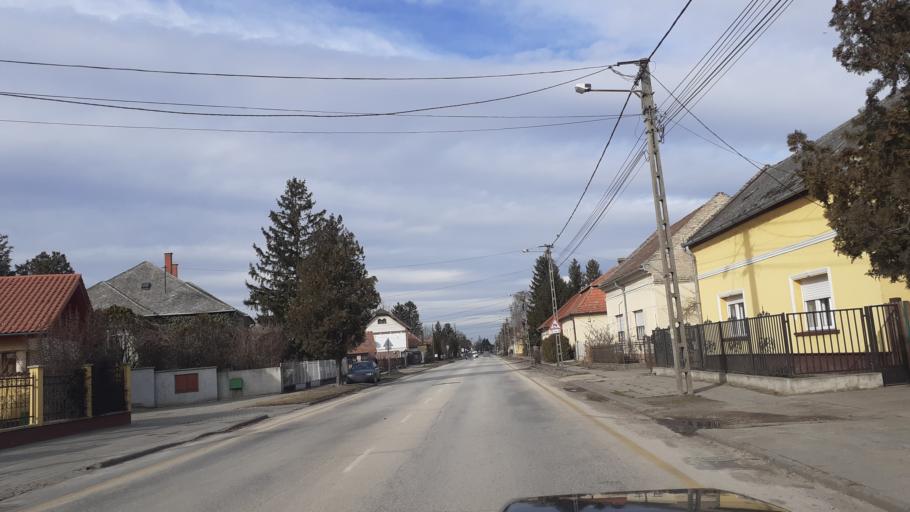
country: HU
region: Fejer
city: Sarbogard
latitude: 46.8905
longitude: 18.6177
